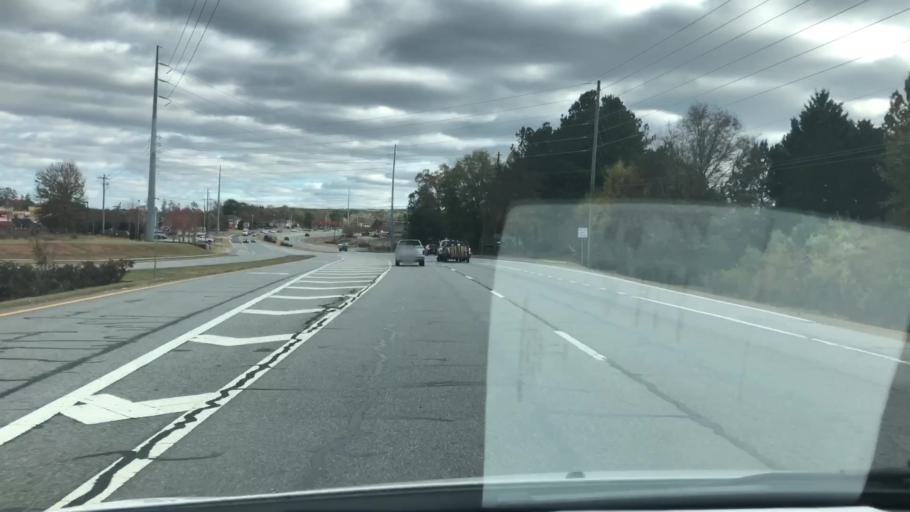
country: US
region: Georgia
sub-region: Fulton County
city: Johns Creek
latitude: 34.0884
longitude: -84.1667
